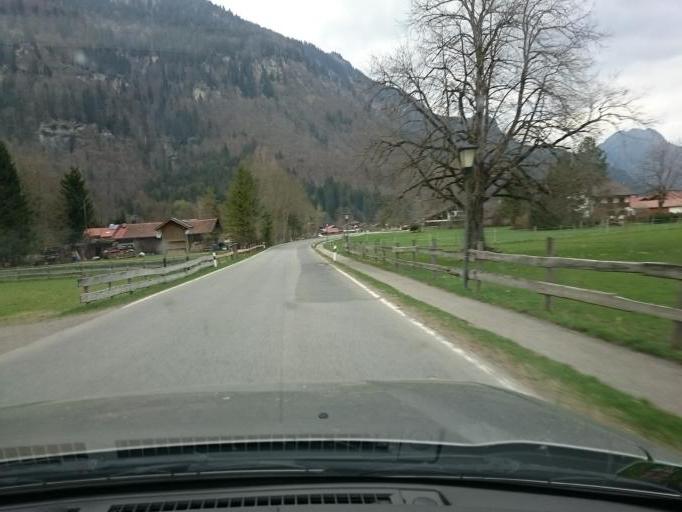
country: DE
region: Bavaria
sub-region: Upper Bavaria
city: Unterammergau
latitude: 47.5712
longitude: 11.0210
